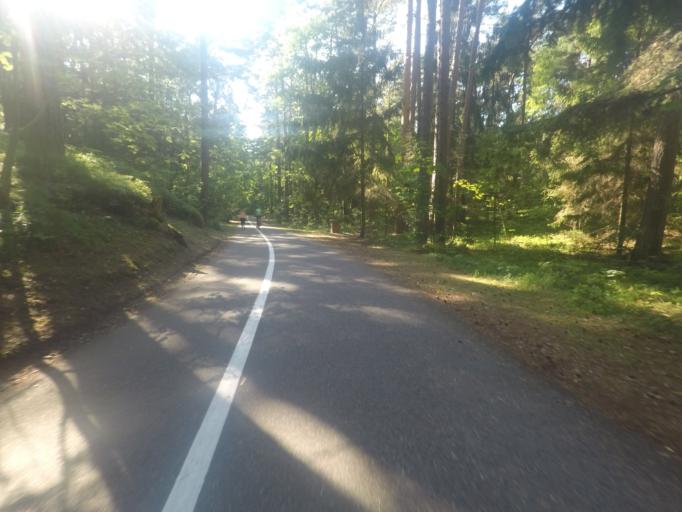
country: LT
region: Klaipedos apskritis
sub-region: Klaipeda
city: Klaipeda
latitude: 55.5454
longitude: 21.1168
